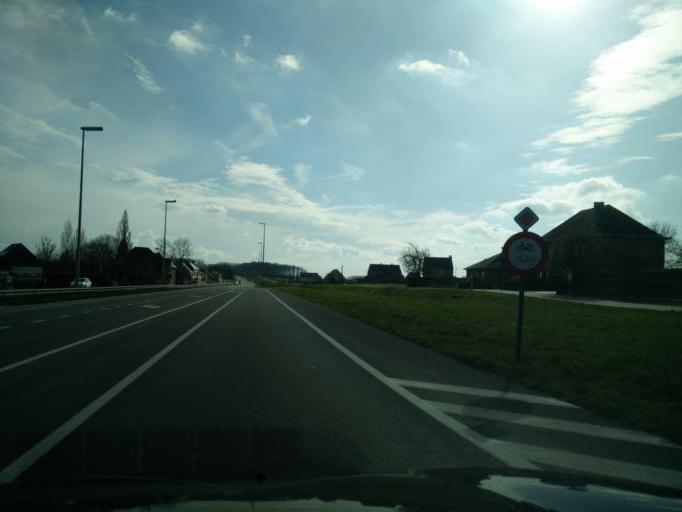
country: BE
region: Flanders
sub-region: Provincie Oost-Vlaanderen
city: Oosterzele
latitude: 50.9233
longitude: 3.8177
